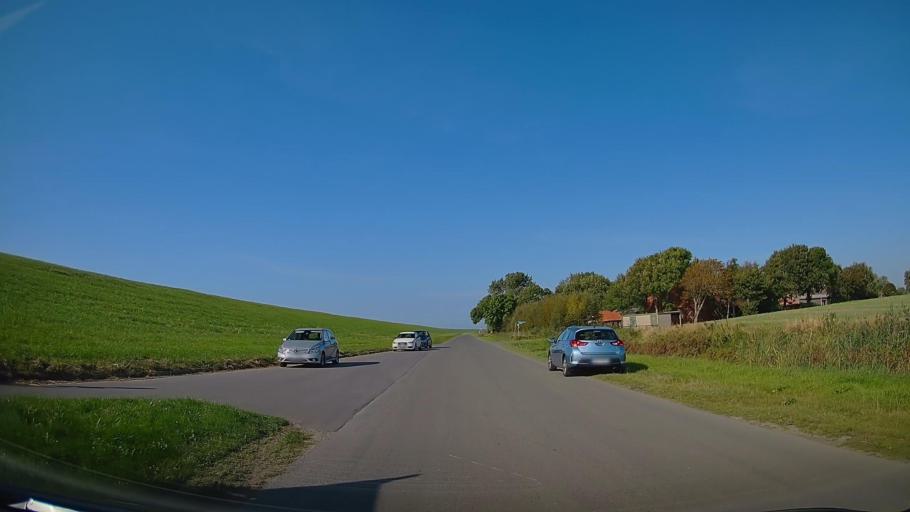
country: DE
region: Lower Saxony
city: Misselwarden
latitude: 53.6712
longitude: 8.4865
